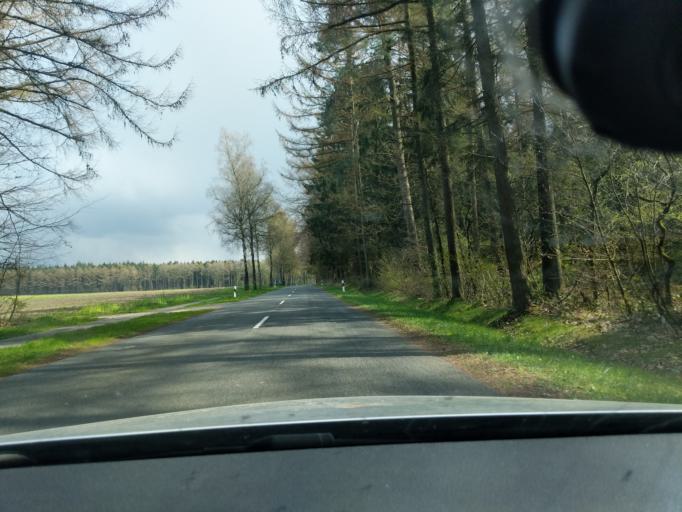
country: DE
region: Lower Saxony
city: Dollern
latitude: 53.5135
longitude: 9.5366
